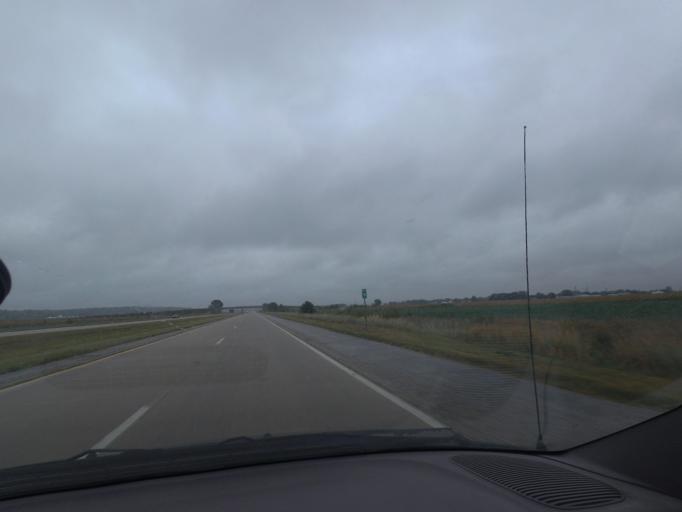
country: US
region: Illinois
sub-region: Adams County
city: Payson
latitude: 39.7215
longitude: -91.2183
